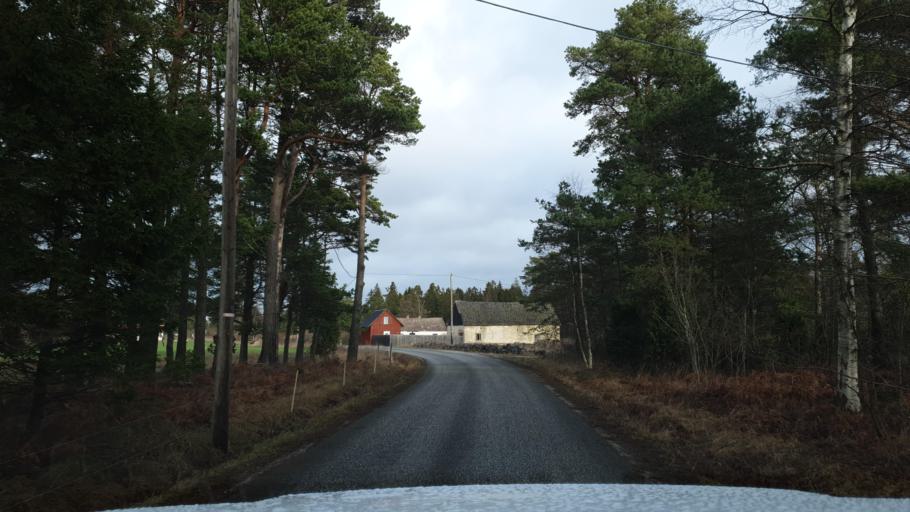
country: SE
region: Gotland
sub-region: Gotland
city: Slite
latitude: 57.3832
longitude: 18.8082
